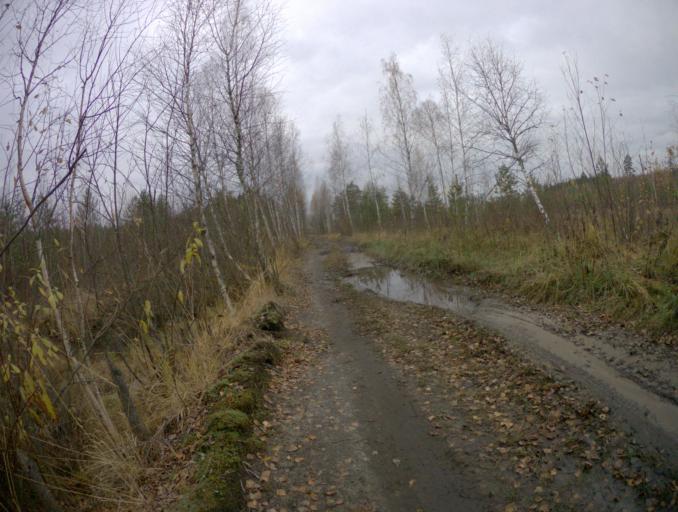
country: RU
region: Moskovskaya
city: Malaya Dubna
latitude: 55.9417
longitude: 38.9602
